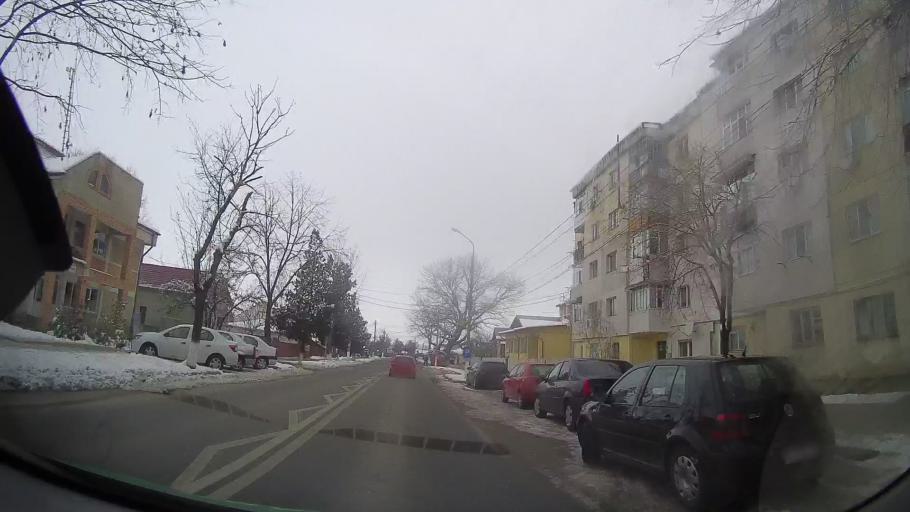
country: RO
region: Vaslui
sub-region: Comuna Negresti
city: Negresti
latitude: 46.8353
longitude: 27.4531
